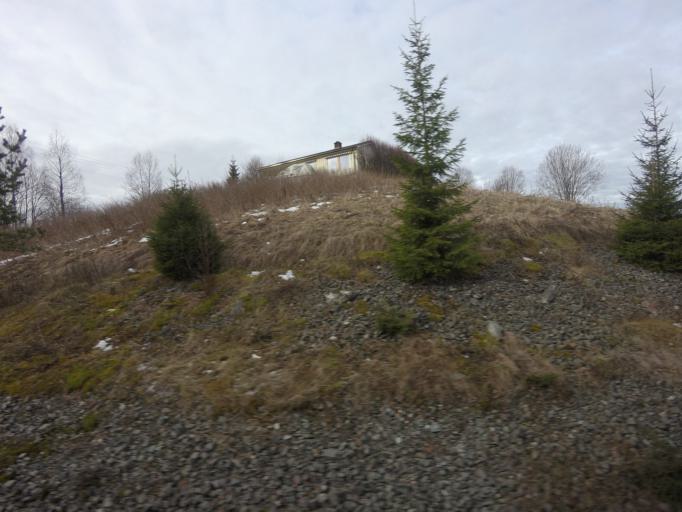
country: NO
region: Akershus
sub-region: Enebakk
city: Flateby
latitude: 59.8583
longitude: 11.2328
